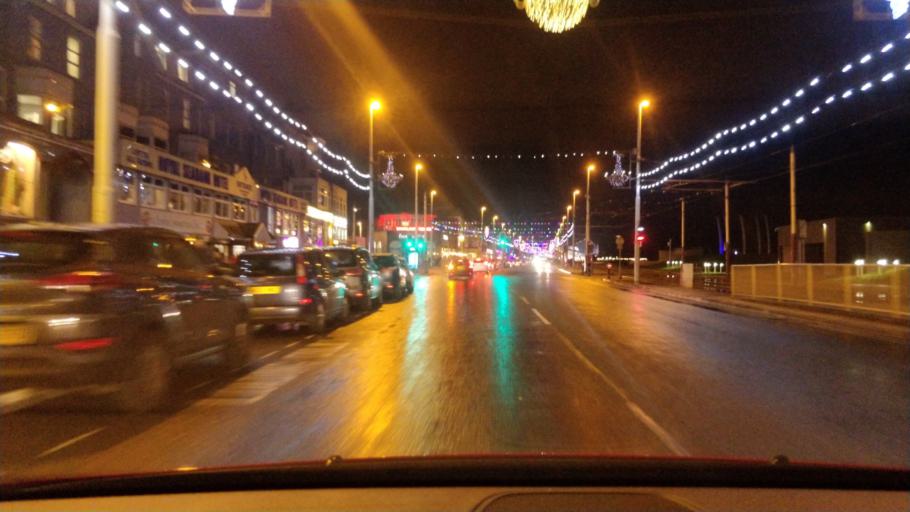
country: GB
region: England
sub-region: Blackpool
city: Blackpool
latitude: 53.8081
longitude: -3.0553
